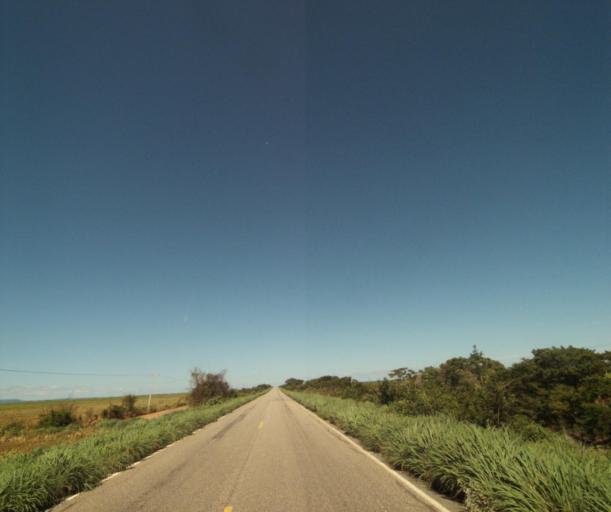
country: BR
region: Bahia
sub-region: Palmas De Monte Alto
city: Palmas de Monte Alto
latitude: -14.2704
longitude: -43.4163
